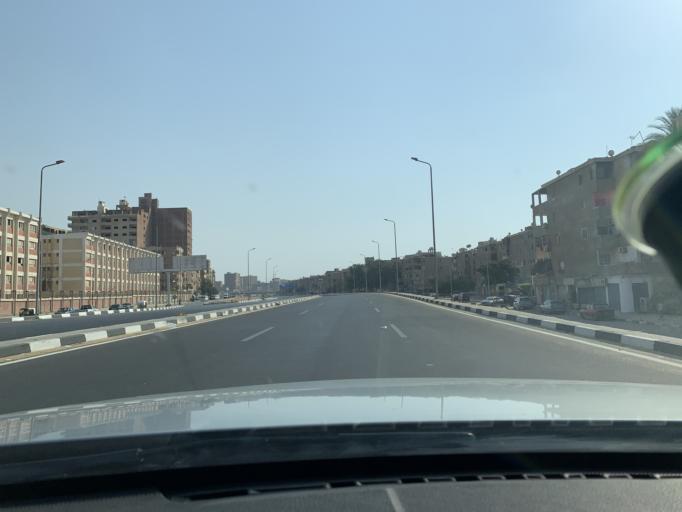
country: EG
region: Muhafazat al Qalyubiyah
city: Al Khankah
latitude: 30.1655
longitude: 31.4096
